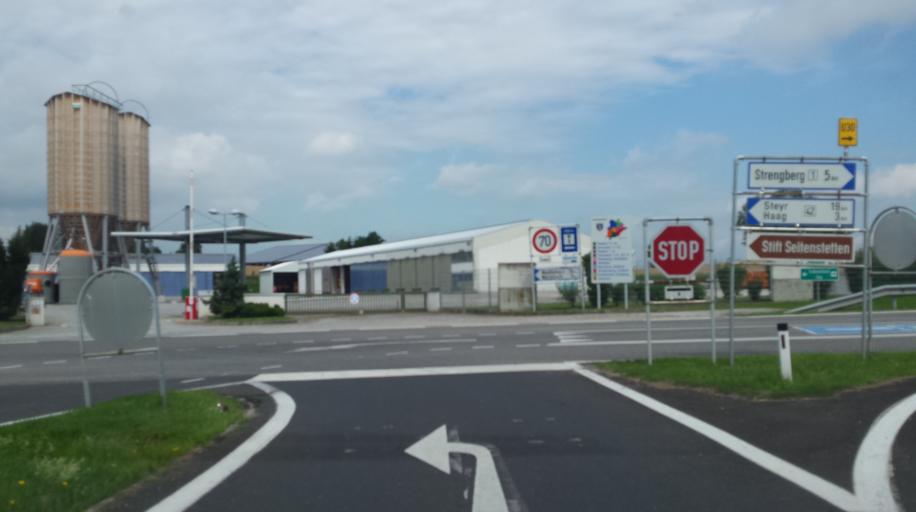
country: AT
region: Lower Austria
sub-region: Politischer Bezirk Amstetten
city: Strengberg
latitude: 48.1328
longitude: 14.5987
